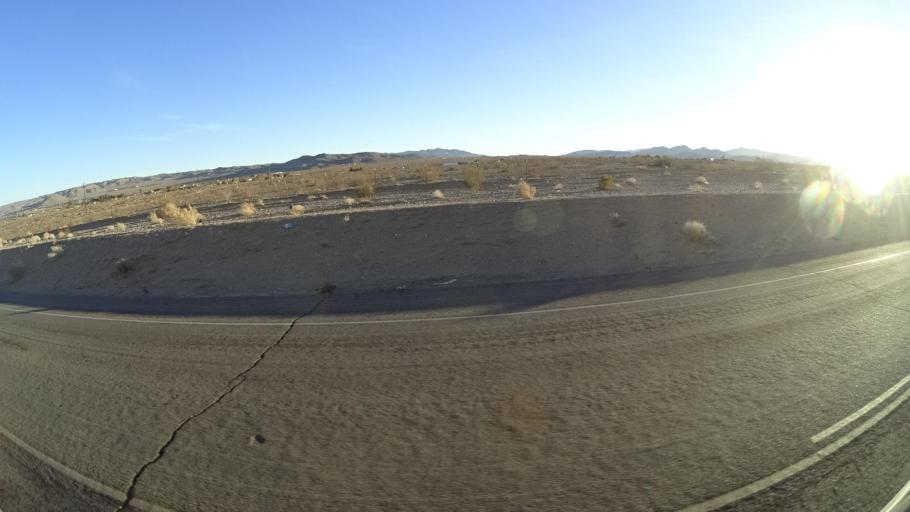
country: US
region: California
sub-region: Kern County
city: Ridgecrest
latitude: 35.6080
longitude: -117.7161
